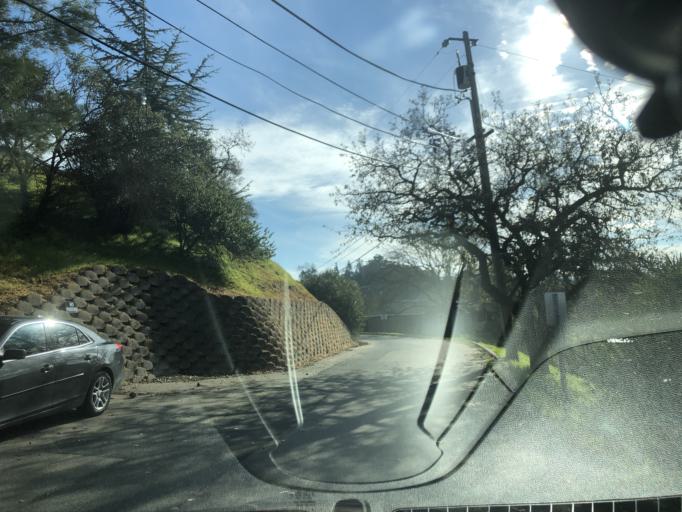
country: US
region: California
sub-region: Contra Costa County
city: Saranap
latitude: 37.8871
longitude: -122.0641
